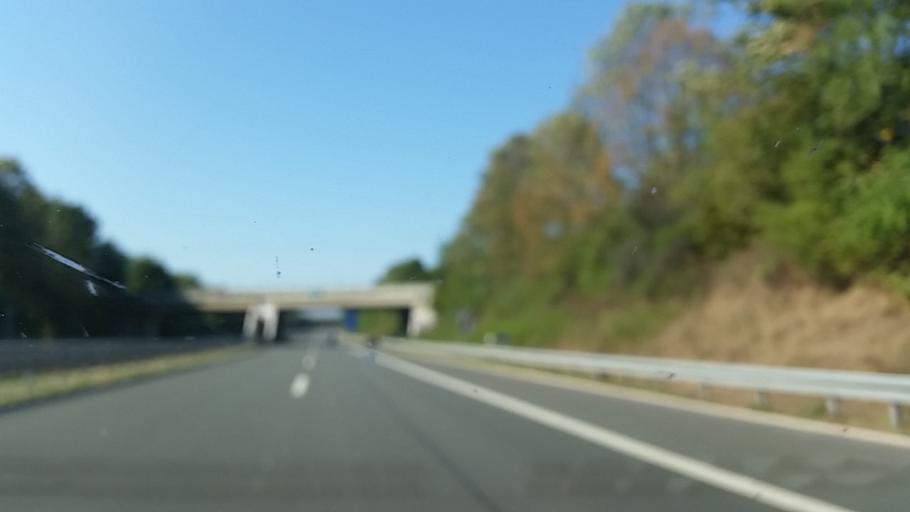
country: DE
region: North Rhine-Westphalia
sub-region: Regierungsbezirk Dusseldorf
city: Langenfeld
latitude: 51.0906
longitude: 6.9472
